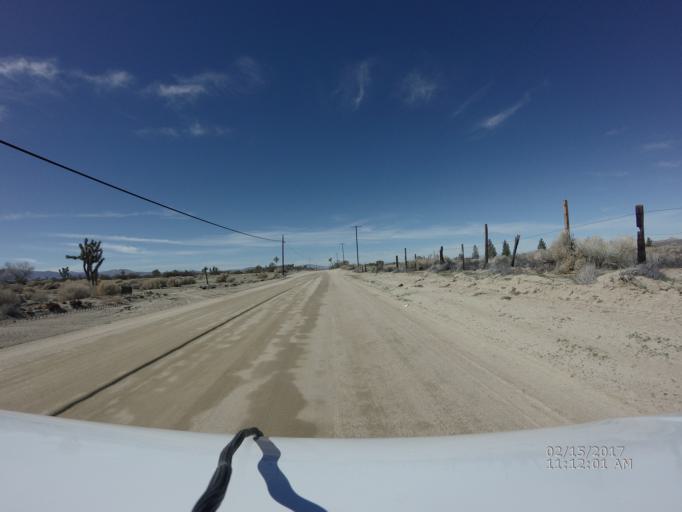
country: US
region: California
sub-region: Los Angeles County
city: Lake Los Angeles
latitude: 34.5874
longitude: -117.8842
